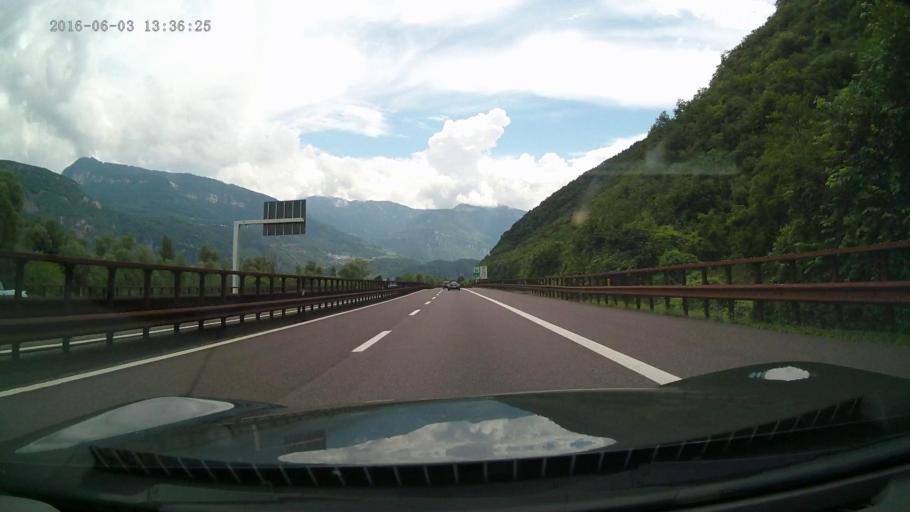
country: IT
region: Trentino-Alto Adige
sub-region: Bolzano
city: Ora
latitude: 46.3722
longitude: 11.2904
